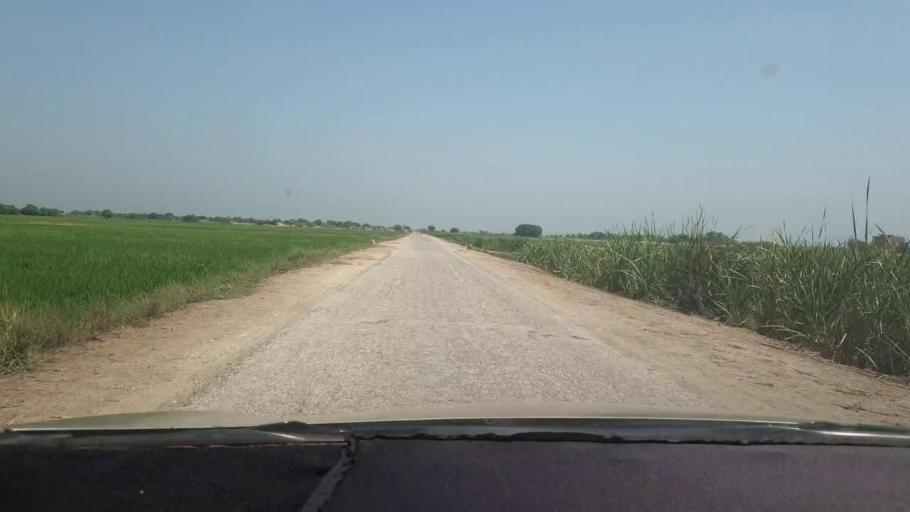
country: PK
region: Sindh
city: Miro Khan
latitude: 27.6879
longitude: 68.0847
